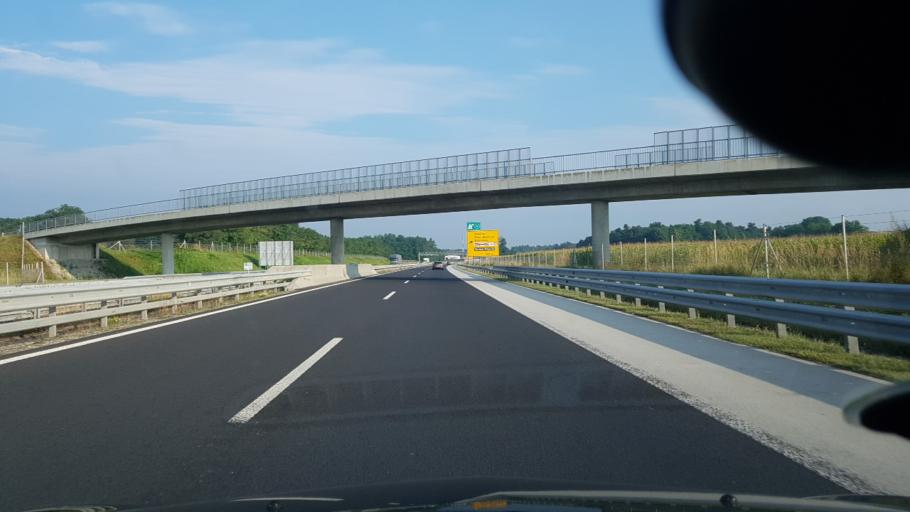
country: SI
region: Hajdina
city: Spodnja Hajdina
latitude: 46.4059
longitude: 15.8204
